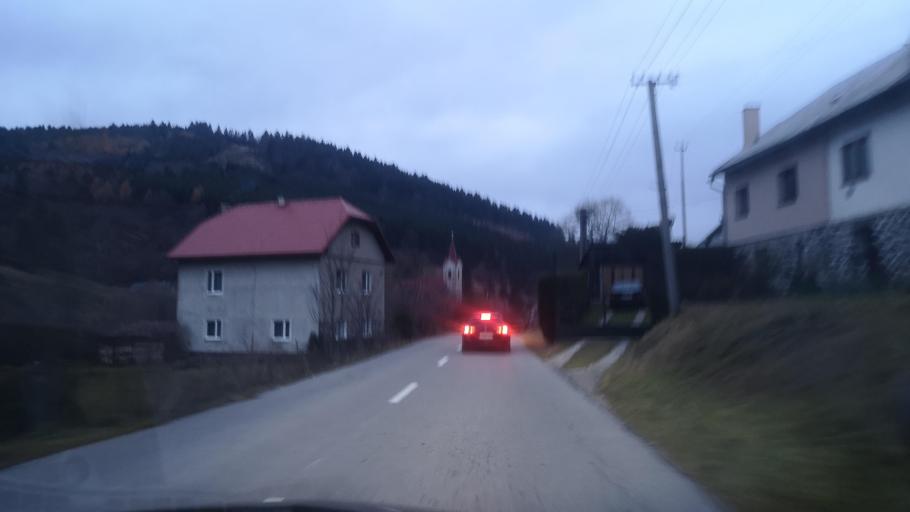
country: SK
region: Banskobystricky
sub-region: Okres Ziar nad Hronom
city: Kremnica
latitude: 48.7622
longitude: 18.9082
